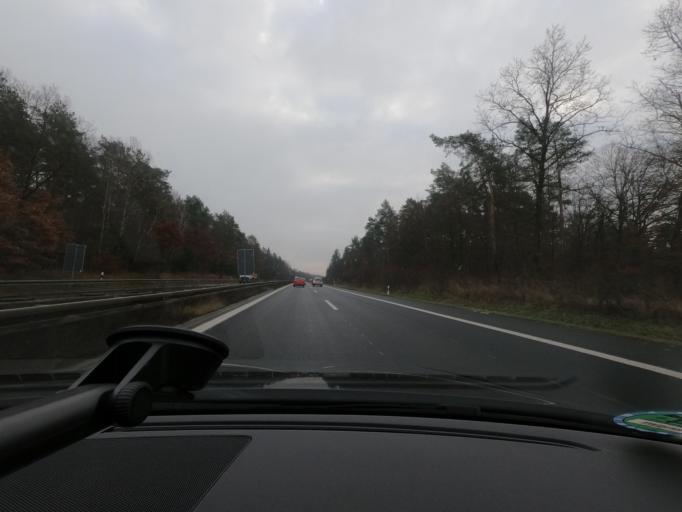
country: DE
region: Bavaria
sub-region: Upper Franconia
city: Kemmern
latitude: 49.9515
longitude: 10.8945
